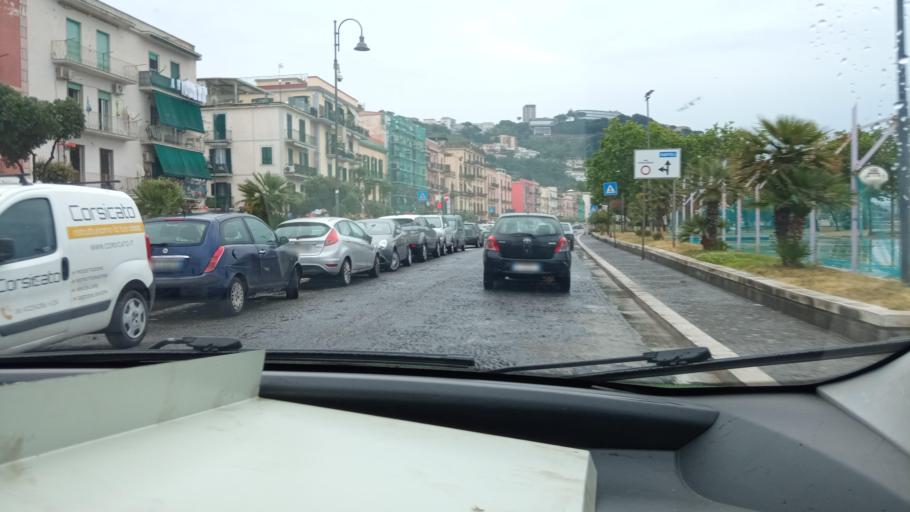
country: IT
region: Campania
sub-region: Provincia di Napoli
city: Pozzuoli
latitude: 40.8213
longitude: 14.1271
